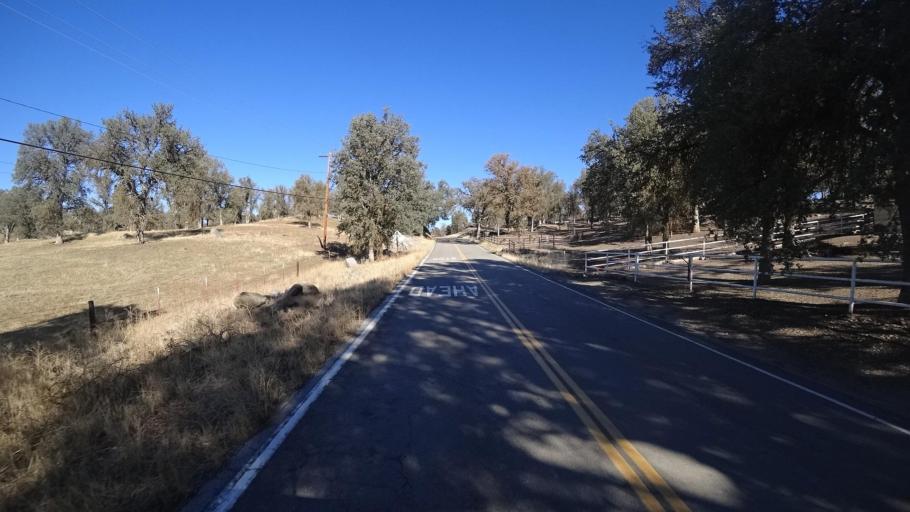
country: US
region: California
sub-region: Kern County
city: Alta Sierra
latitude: 35.7274
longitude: -118.7221
